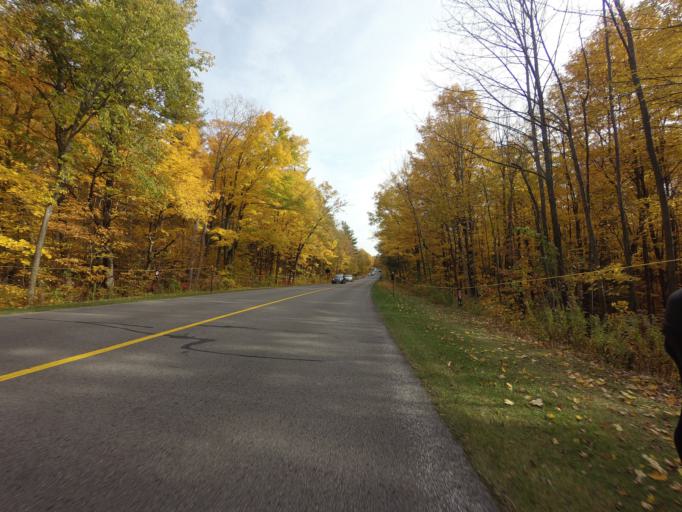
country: CA
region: Quebec
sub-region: Outaouais
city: Gatineau
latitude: 45.4684
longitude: -75.8161
